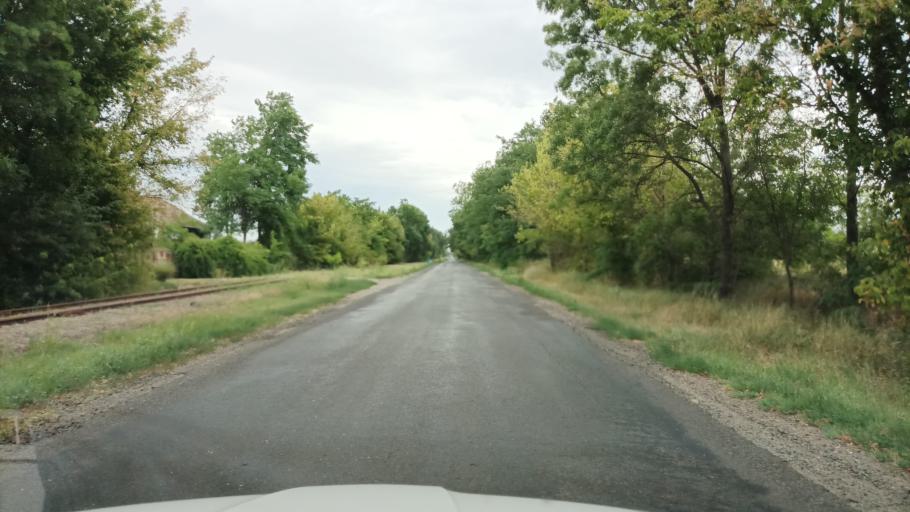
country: HU
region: Pest
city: Taborfalva
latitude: 47.0872
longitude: 19.4580
